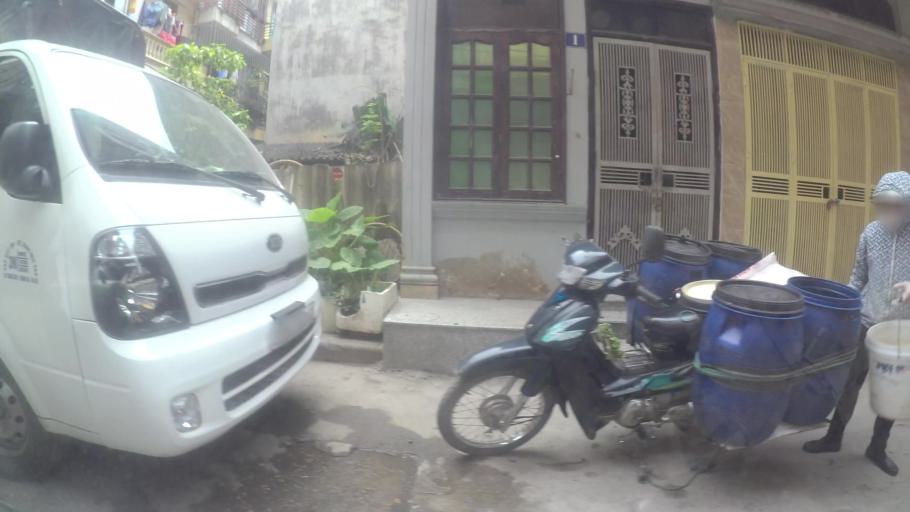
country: VN
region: Ha Noi
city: Ha Dong
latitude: 20.9727
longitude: 105.7661
